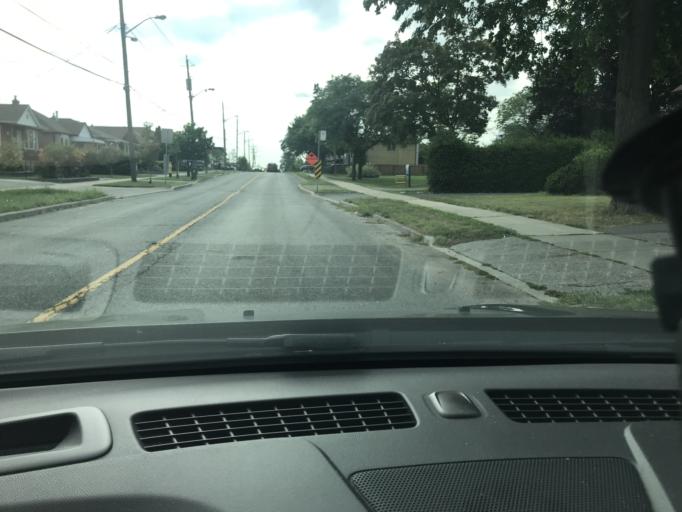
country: CA
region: Ontario
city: Toronto
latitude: 43.7225
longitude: -79.4525
